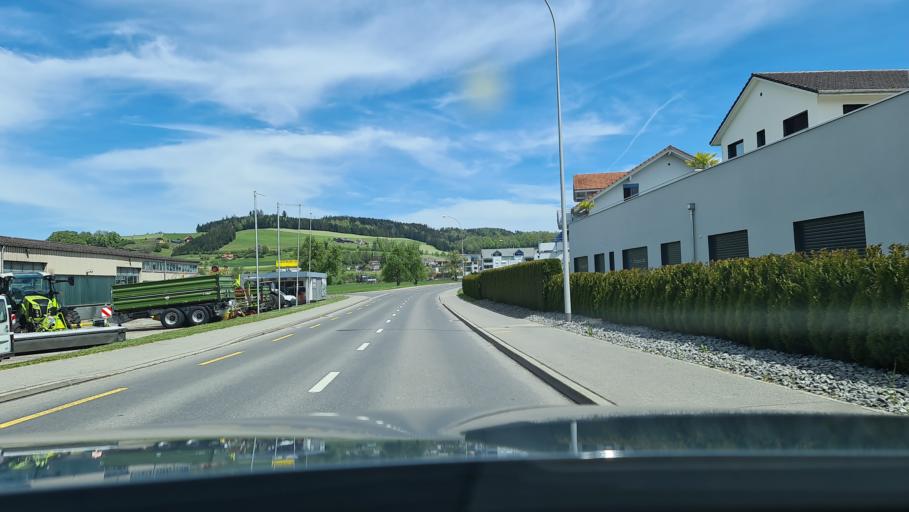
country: CH
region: Lucerne
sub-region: Sursee District
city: Buttisholz
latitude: 47.1088
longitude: 8.0858
